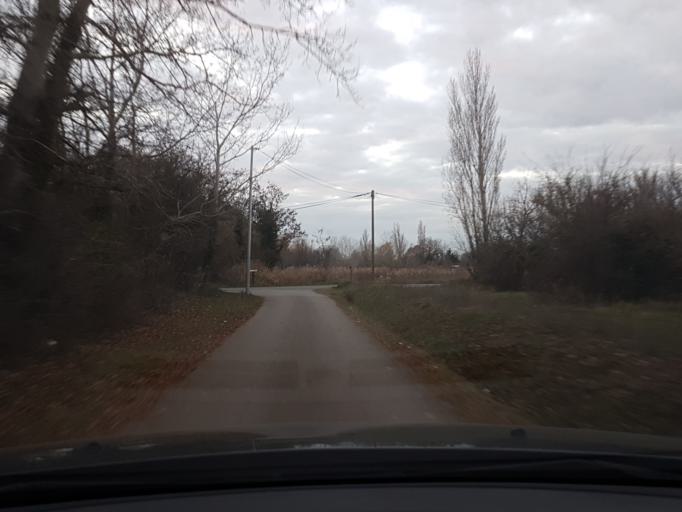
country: FR
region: Provence-Alpes-Cote d'Azur
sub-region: Departement du Vaucluse
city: Loriol-du-Comtat
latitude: 44.0871
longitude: 4.9955
